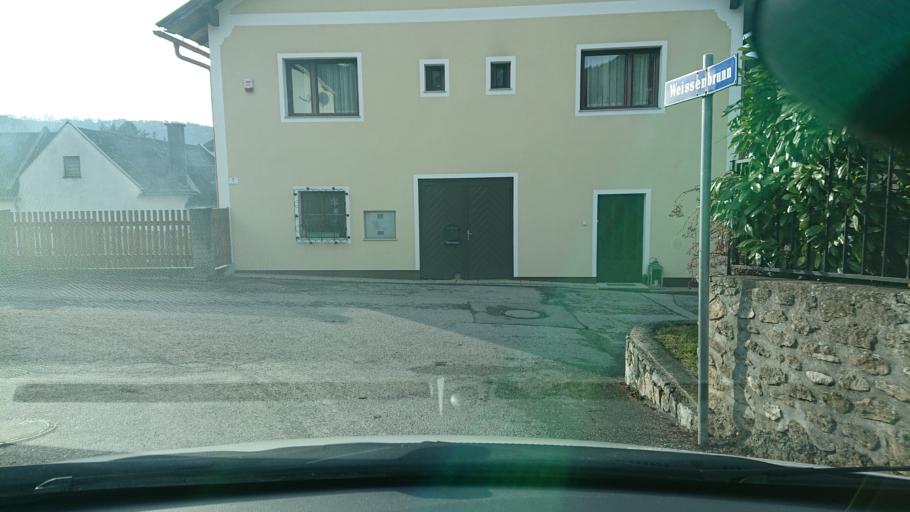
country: AT
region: Lower Austria
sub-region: Politischer Bezirk Baden
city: Hernstein
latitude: 47.8960
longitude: 16.1047
